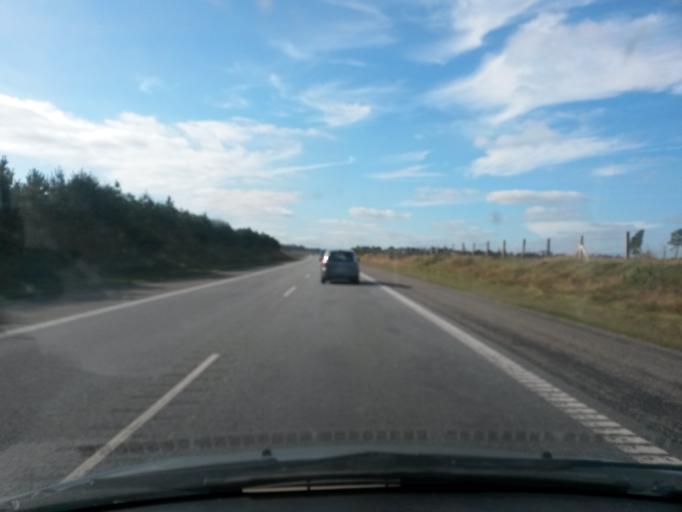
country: DK
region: Central Jutland
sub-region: Herning Kommune
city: Snejbjerg
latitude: 56.1877
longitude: 8.9346
